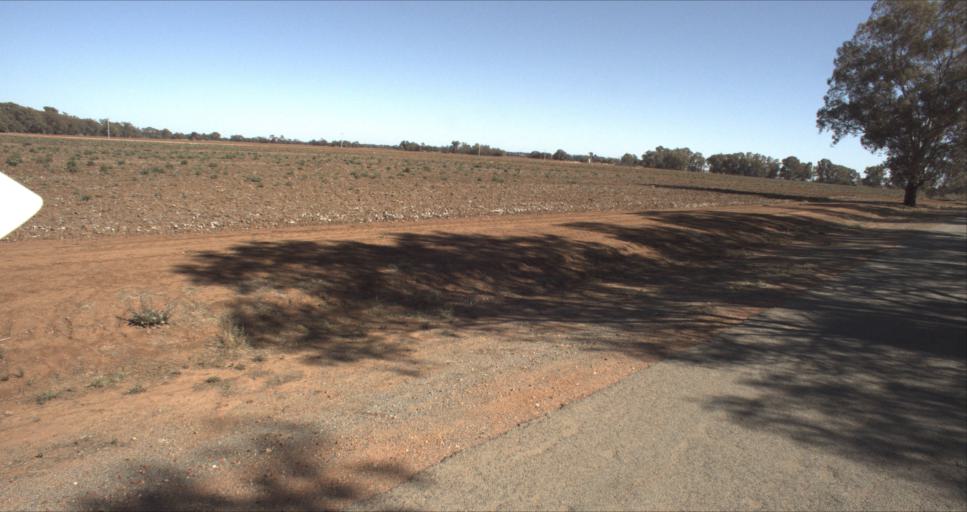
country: AU
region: New South Wales
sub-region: Leeton
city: Leeton
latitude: -34.6116
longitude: 146.2599
